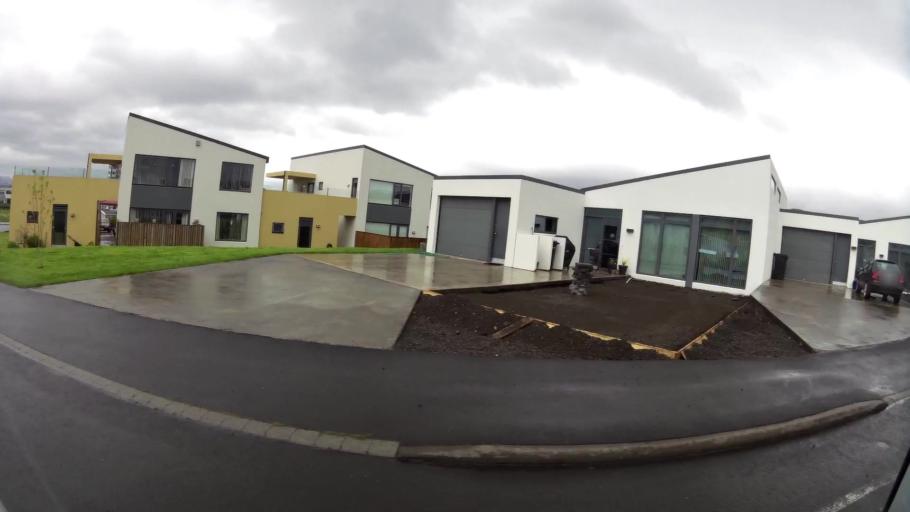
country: IS
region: Northeast
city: Akureyri
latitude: 65.6633
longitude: -18.1034
